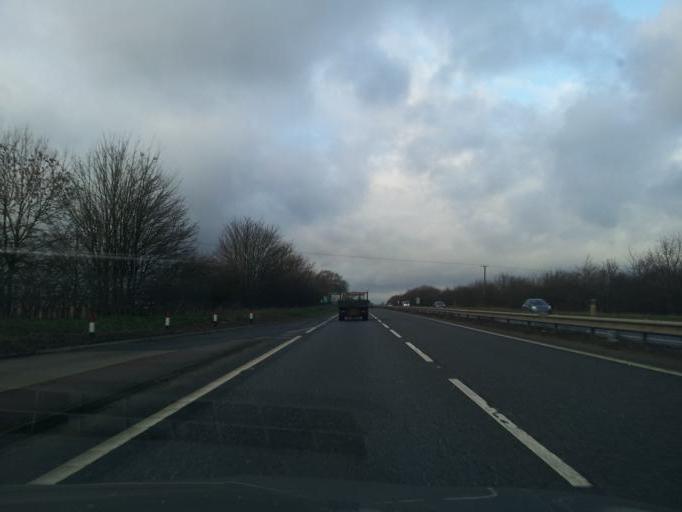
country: GB
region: England
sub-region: Norfolk
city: Costessey
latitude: 52.6429
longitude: 1.1917
